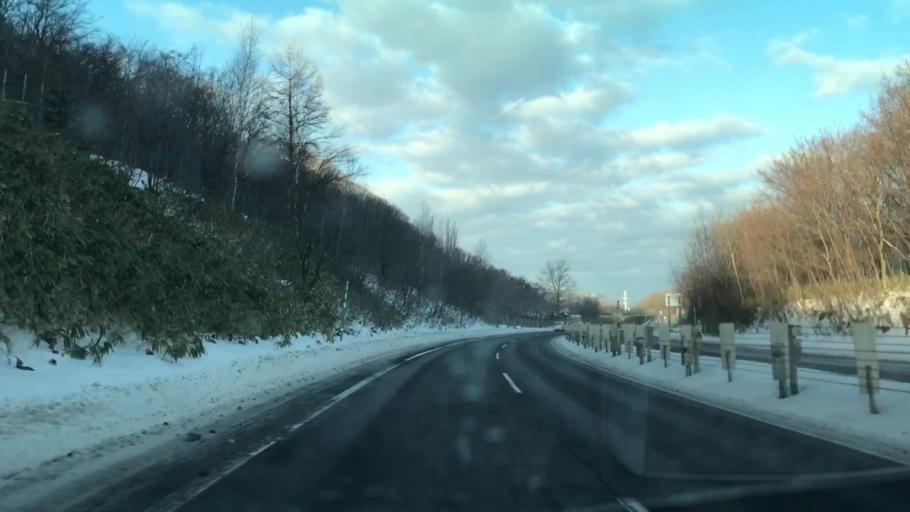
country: JP
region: Hokkaido
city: Sapporo
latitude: 43.1263
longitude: 141.1977
